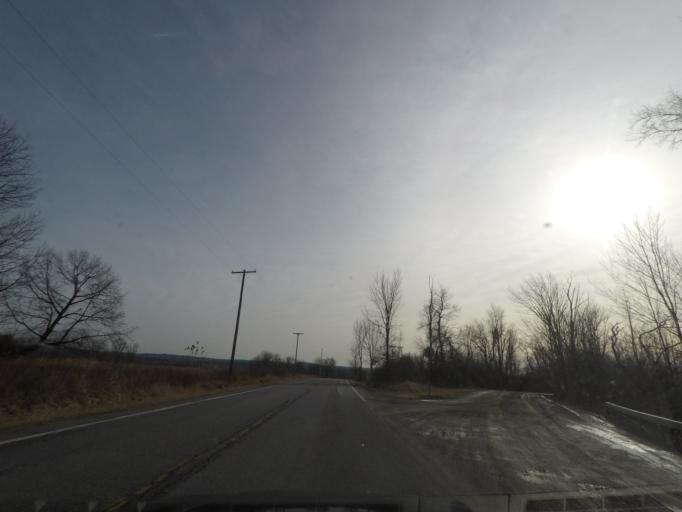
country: US
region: New York
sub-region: Saratoga County
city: Stillwater
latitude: 42.9774
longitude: -73.6362
